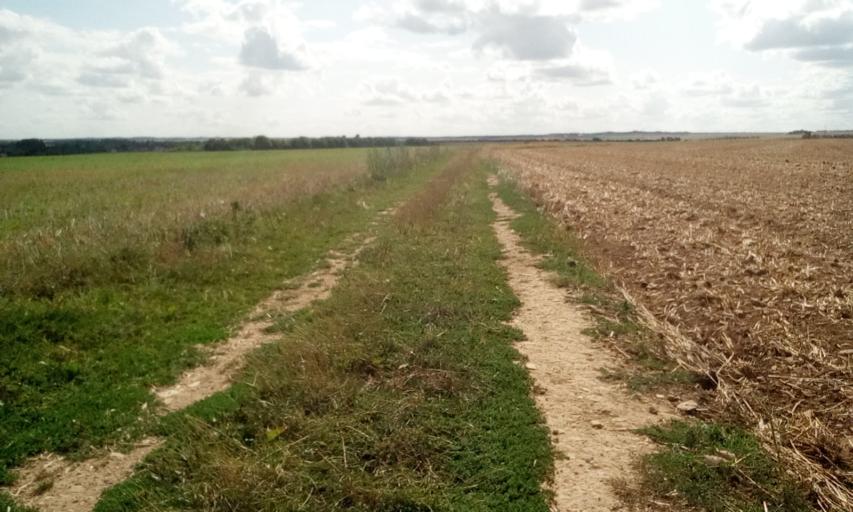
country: FR
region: Lower Normandy
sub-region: Departement du Calvados
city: Saint-Sylvain
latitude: 49.0750
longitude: -0.2072
